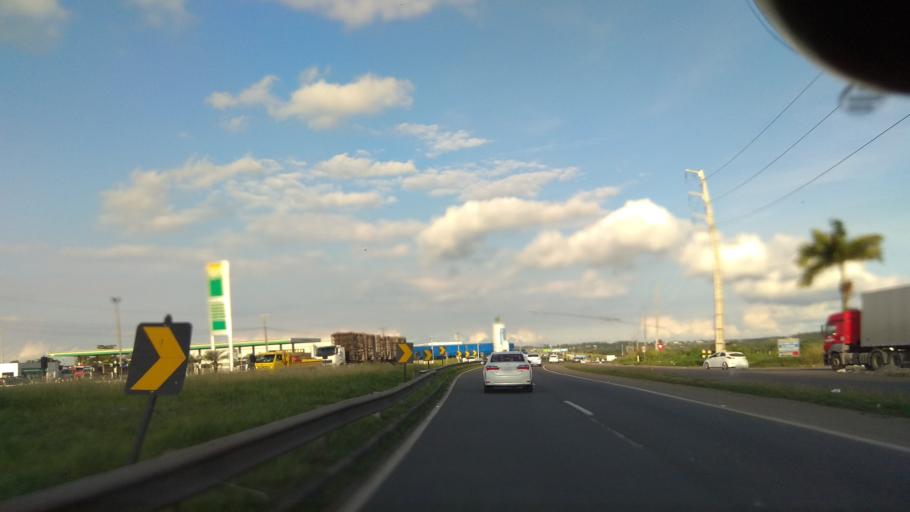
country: BR
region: Bahia
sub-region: Conceicao Do Jacuipe
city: Conceicao do Jacuipe
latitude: -12.3397
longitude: -38.8467
